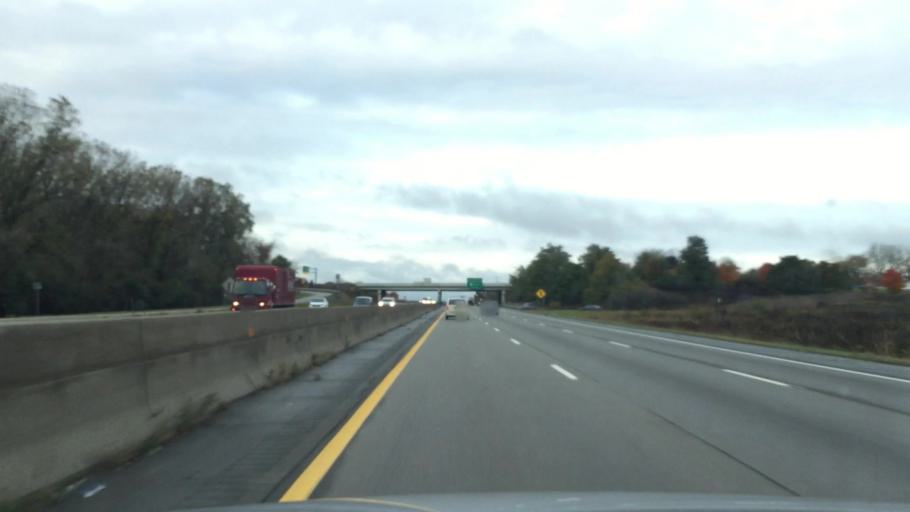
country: US
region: Michigan
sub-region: Washtenaw County
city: Ypsilanti
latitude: 42.2298
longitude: -83.6132
